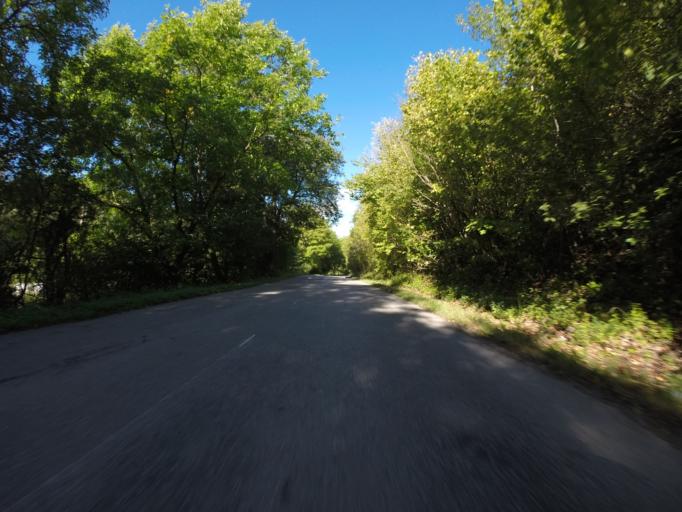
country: SK
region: Nitriansky
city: Ilava
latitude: 48.9680
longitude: 18.3560
